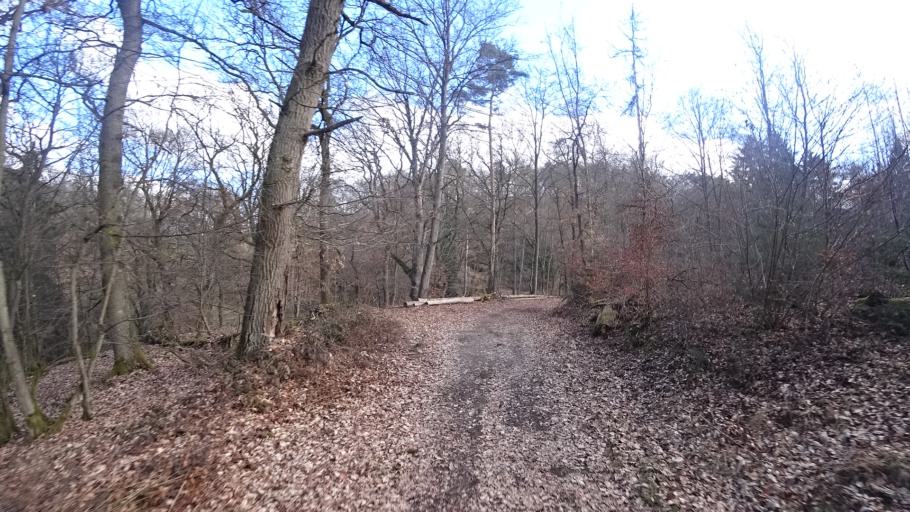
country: DE
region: Rheinland-Pfalz
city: Reichenberg
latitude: 50.1443
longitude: 7.7526
